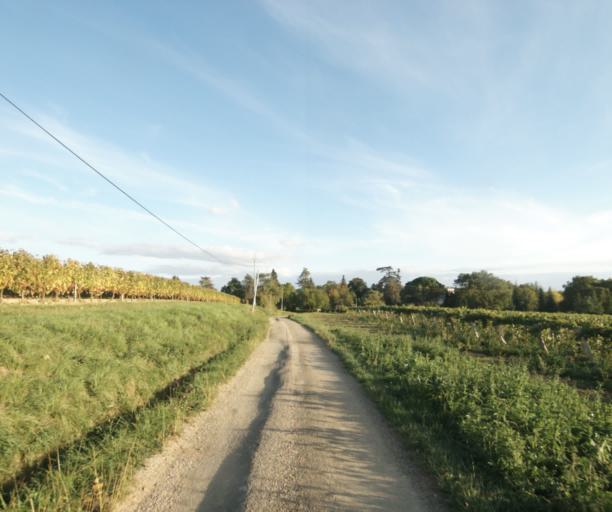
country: FR
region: Midi-Pyrenees
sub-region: Departement du Gers
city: Gondrin
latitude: 43.8645
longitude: 0.2946
